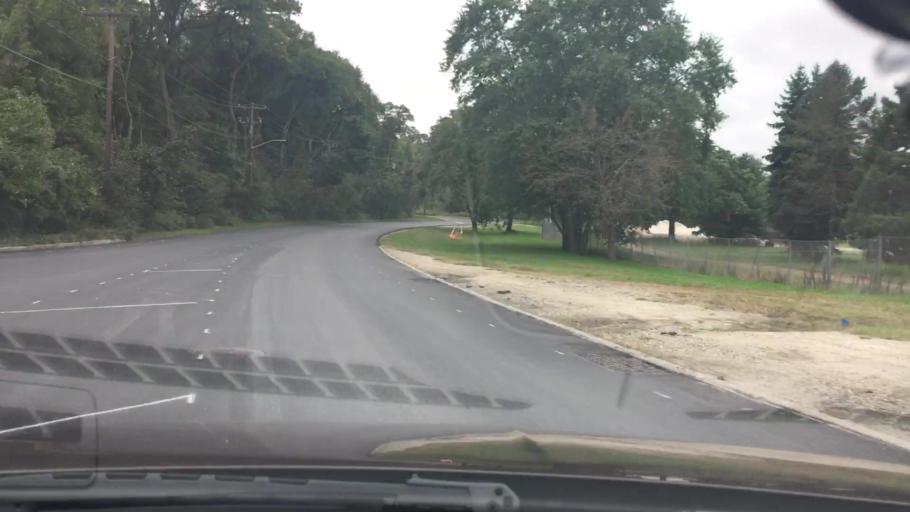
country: US
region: New York
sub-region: Nassau County
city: Old Bethpage
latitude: 40.7494
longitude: -73.4499
